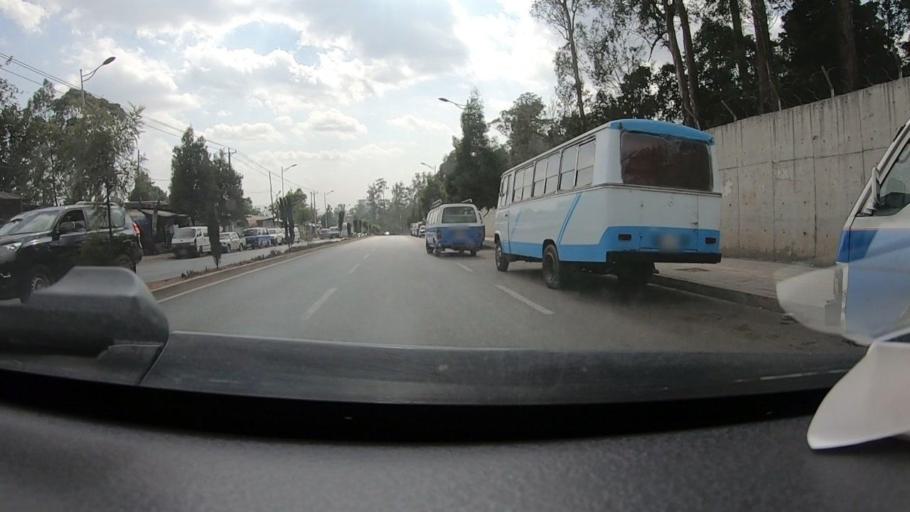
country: ET
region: Adis Abeba
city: Addis Ababa
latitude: 9.0545
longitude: 38.7730
